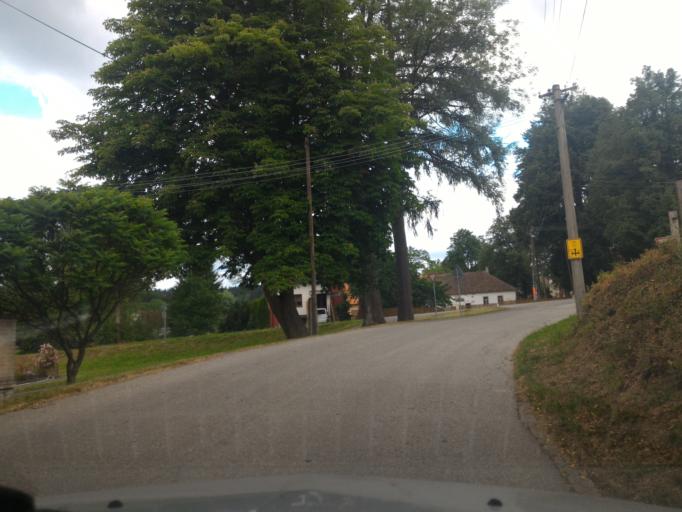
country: CZ
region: Vysocina
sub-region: Okres Jihlava
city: Telc
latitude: 49.2191
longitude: 15.3954
